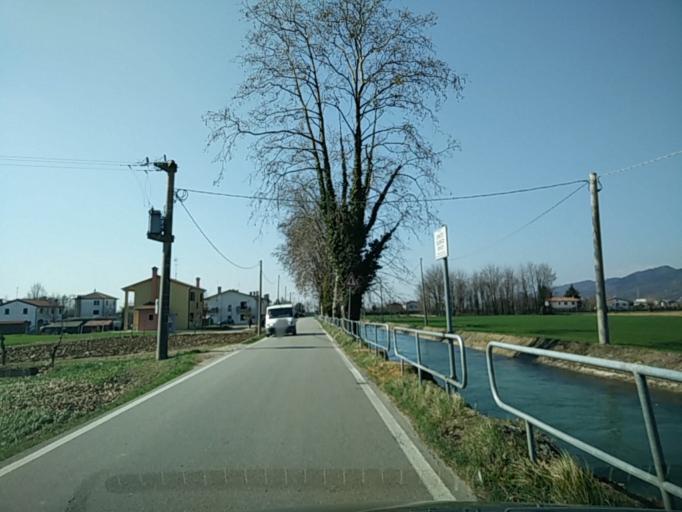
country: IT
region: Veneto
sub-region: Provincia di Treviso
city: Crocetta-Nogare
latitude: 45.8192
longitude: 12.0293
